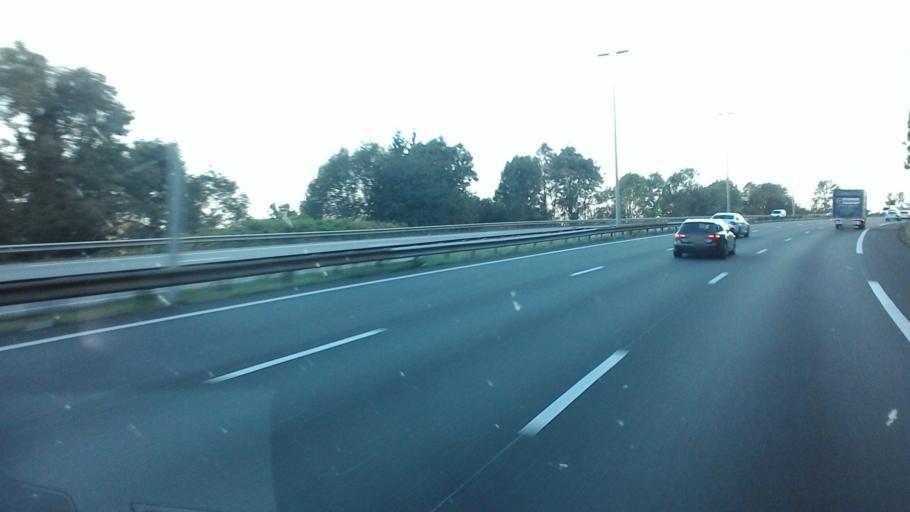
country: FR
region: Lorraine
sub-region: Departement de Meurthe-et-Moselle
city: Champigneulles
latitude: 48.7250
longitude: 6.1691
